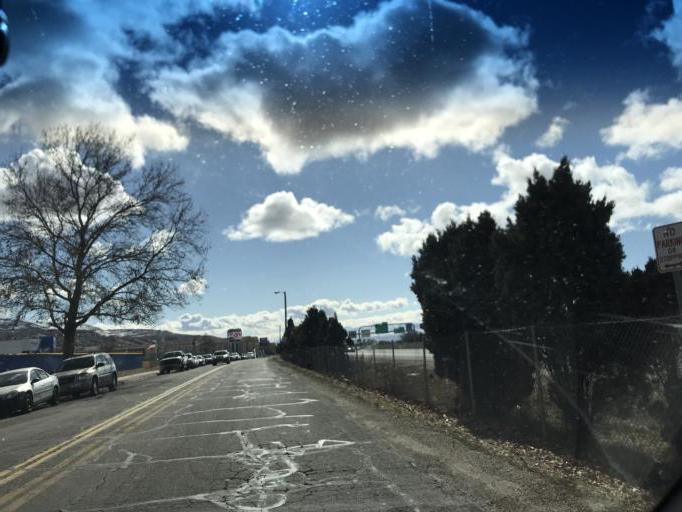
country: US
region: Utah
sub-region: Davis County
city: Woods Cross
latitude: 40.8674
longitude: -111.8977
